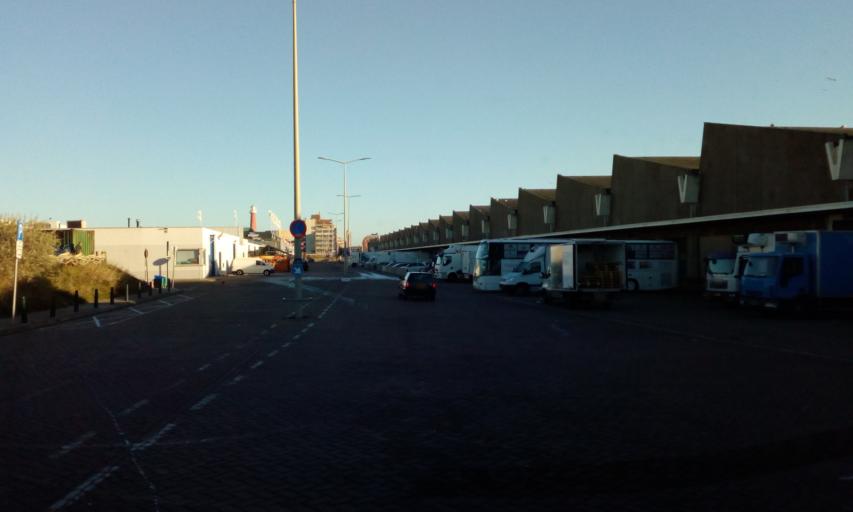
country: NL
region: South Holland
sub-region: Gemeente Den Haag
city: Scheveningen
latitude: 52.0998
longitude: 4.2630
